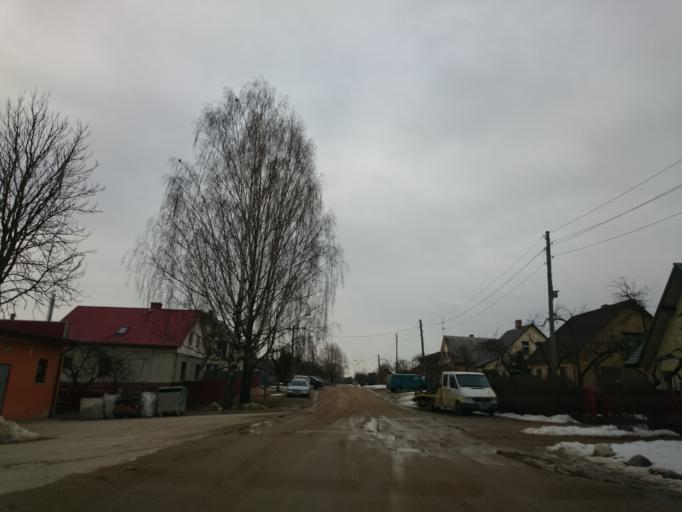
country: LV
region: Cesu Rajons
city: Cesis
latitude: 57.3189
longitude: 25.2669
